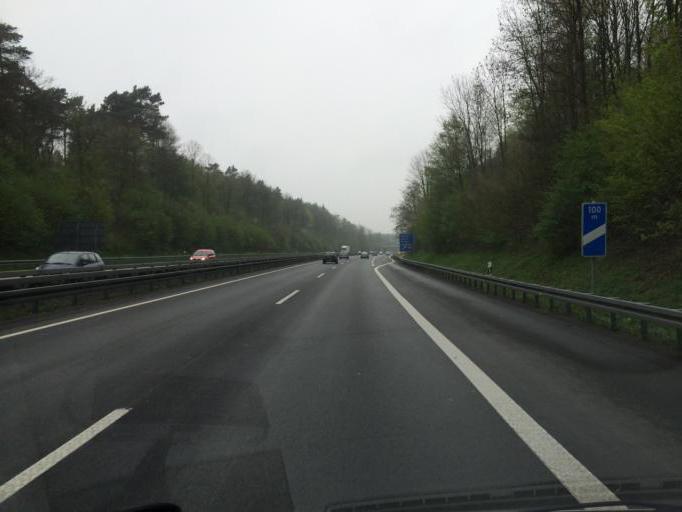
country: DE
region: North Rhine-Westphalia
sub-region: Regierungsbezirk Munster
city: Haltern
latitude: 51.7294
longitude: 7.1490
